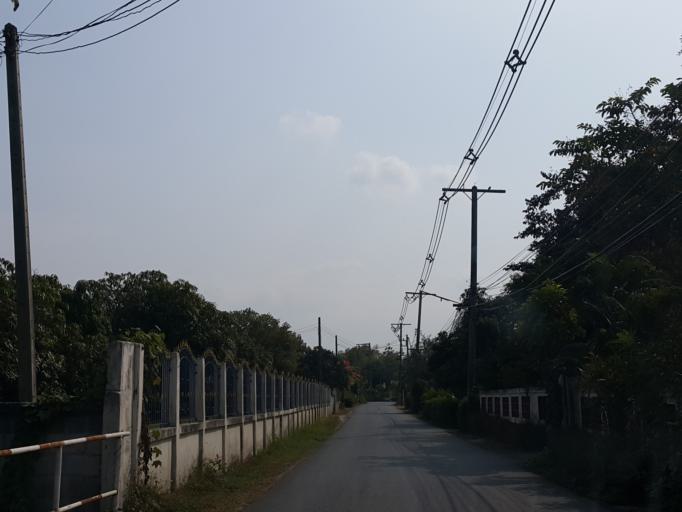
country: TH
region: Chiang Mai
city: San Kamphaeng
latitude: 18.8092
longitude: 99.1246
